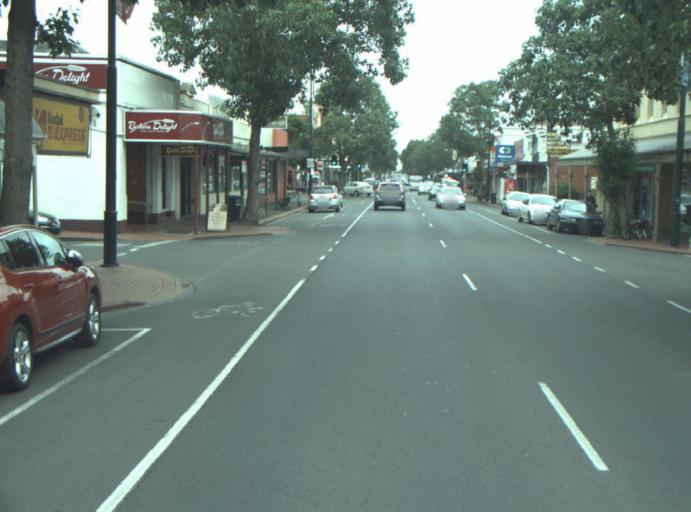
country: AU
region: Victoria
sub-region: Greater Geelong
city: Geelong West
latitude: -38.1418
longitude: 144.3481
